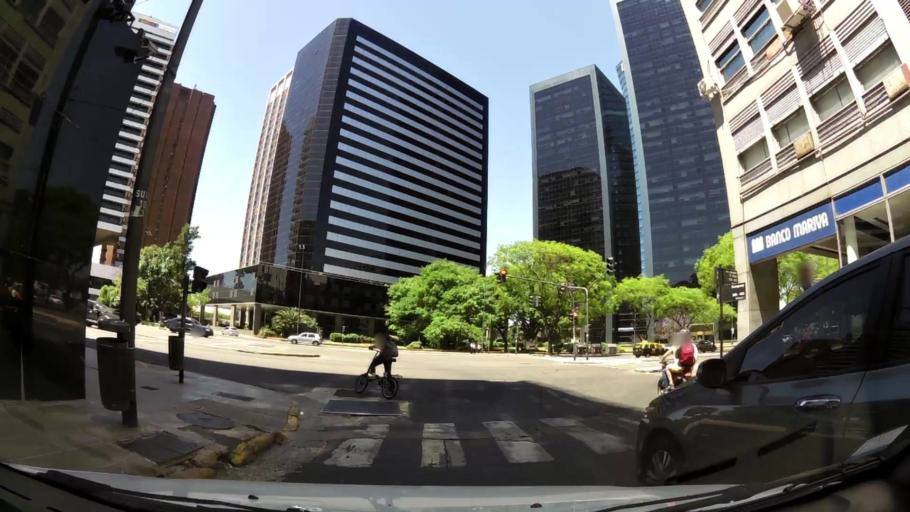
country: AR
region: Buenos Aires F.D.
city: Buenos Aires
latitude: -34.5972
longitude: -58.3724
